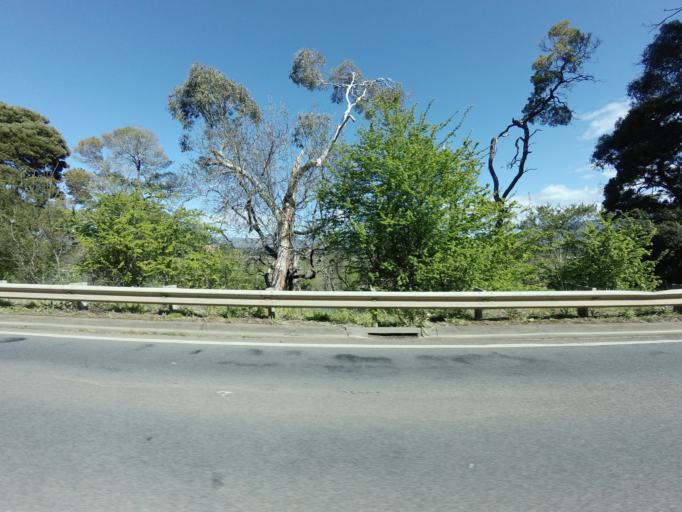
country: AU
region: Tasmania
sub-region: Derwent Valley
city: New Norfolk
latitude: -42.7328
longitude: 146.9715
